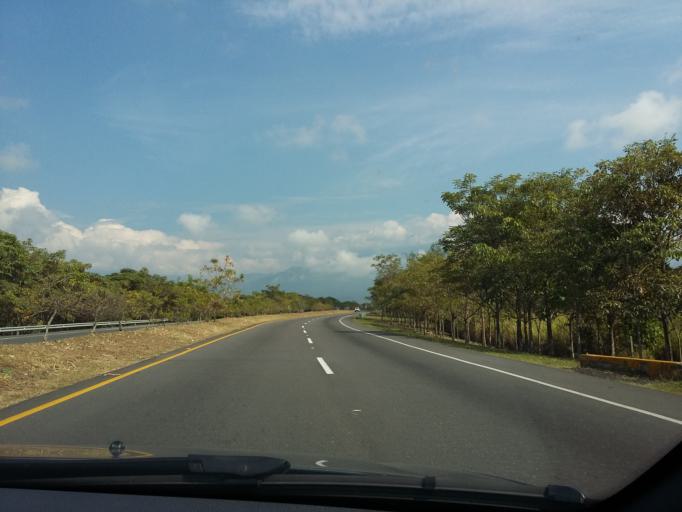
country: CO
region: Tolima
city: Ibague
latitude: 4.3939
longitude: -75.1685
